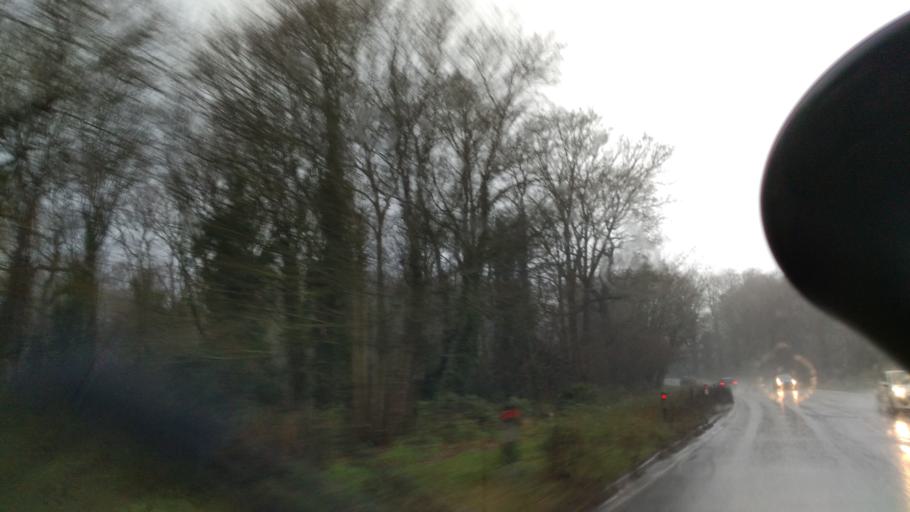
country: GB
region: England
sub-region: West Sussex
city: Arundel
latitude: 50.8561
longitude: -0.5786
